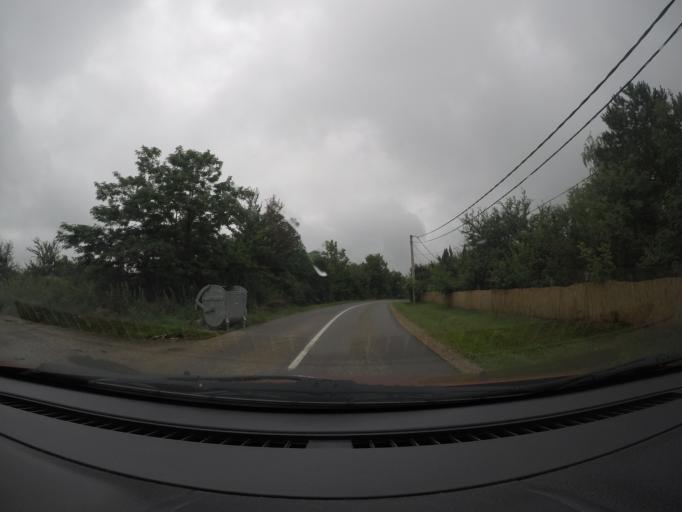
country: RS
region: Central Serbia
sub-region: Belgrade
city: Sopot
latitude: 44.5216
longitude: 20.5359
